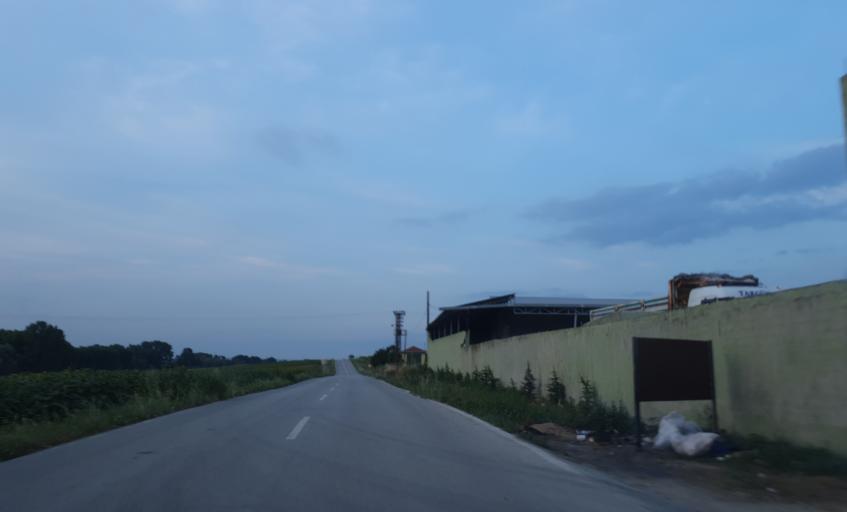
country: TR
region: Tekirdag
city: Beyazkoy
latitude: 41.3948
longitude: 27.6319
